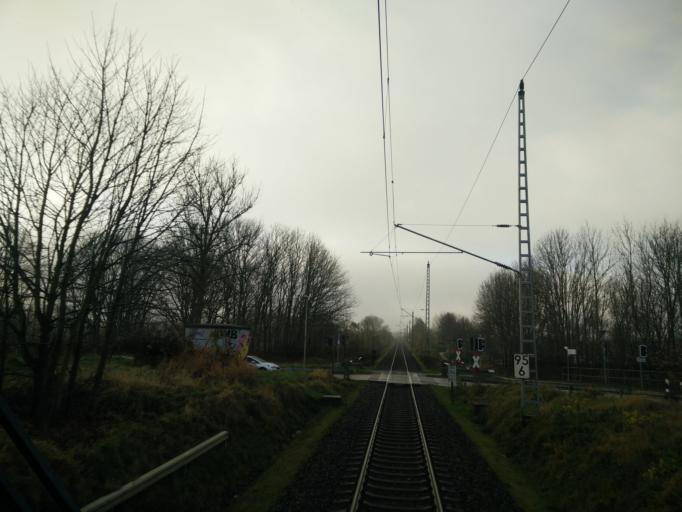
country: DE
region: Mecklenburg-Vorpommern
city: Wismar
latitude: 53.8736
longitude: 11.4700
